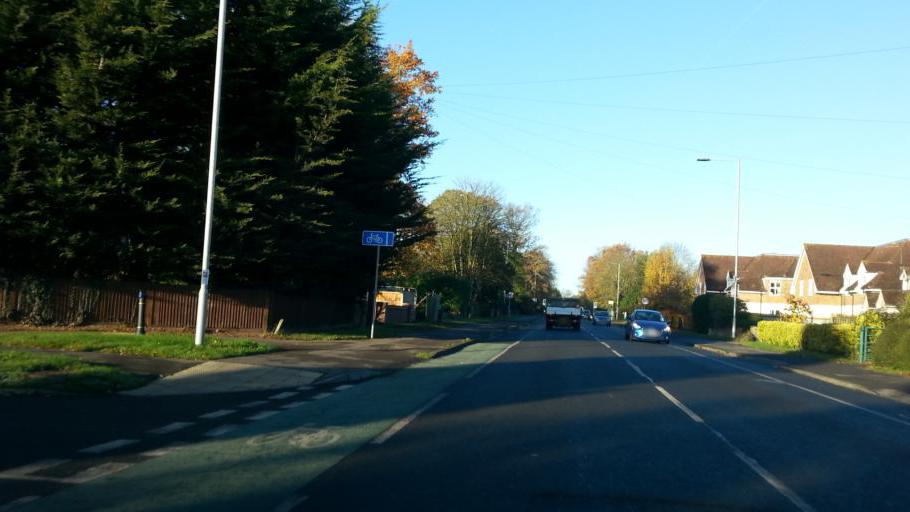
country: GB
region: England
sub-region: Wokingham
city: Earley
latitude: 51.4408
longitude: -0.9238
